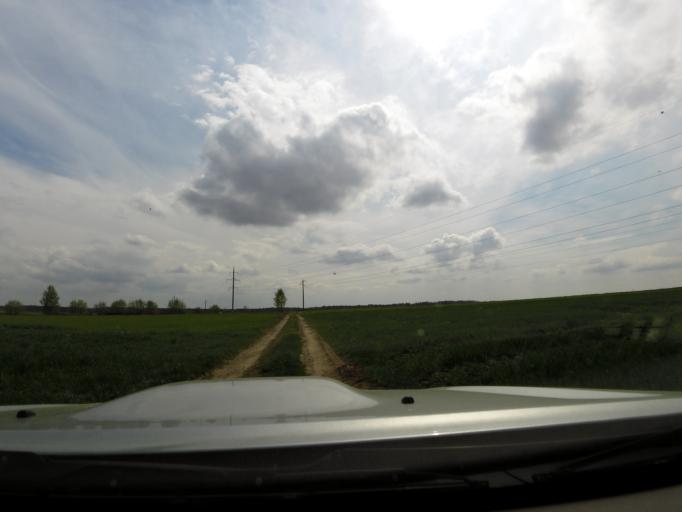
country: LT
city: Salcininkai
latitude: 54.4178
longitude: 25.3113
